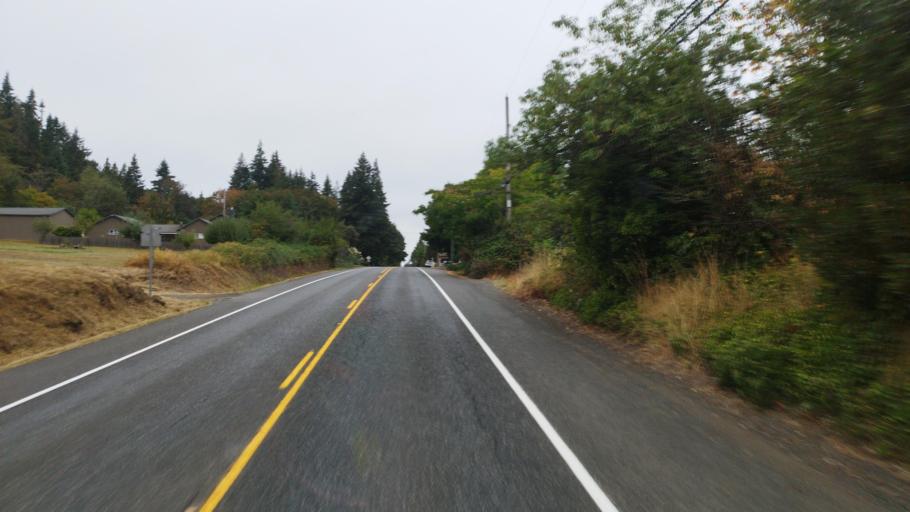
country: US
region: Oregon
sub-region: Columbia County
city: Rainier
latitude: 46.0767
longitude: -122.9083
